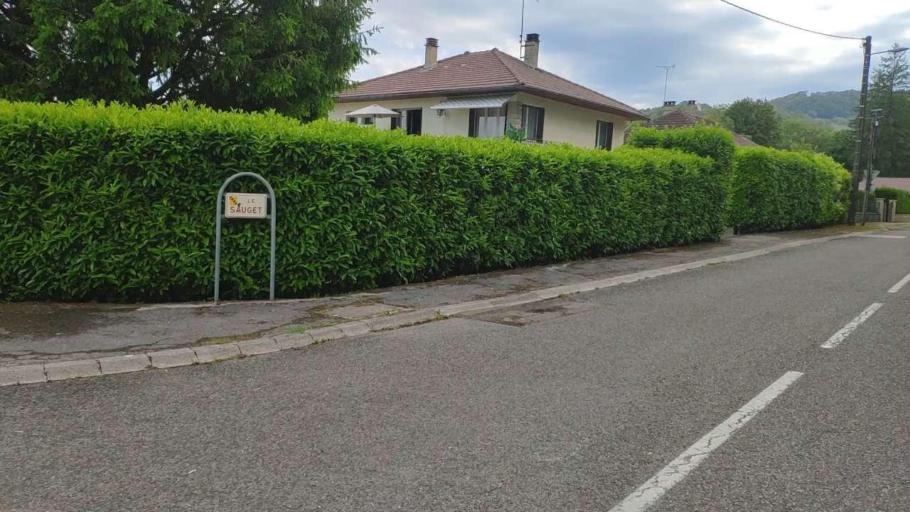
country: FR
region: Franche-Comte
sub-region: Departement du Jura
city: Perrigny
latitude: 46.7575
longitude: 5.6098
